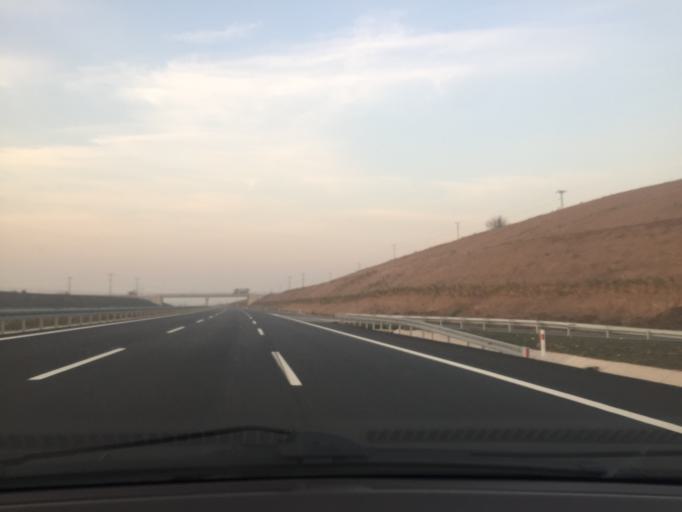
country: TR
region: Bursa
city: Karacabey
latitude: 40.2453
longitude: 28.4357
